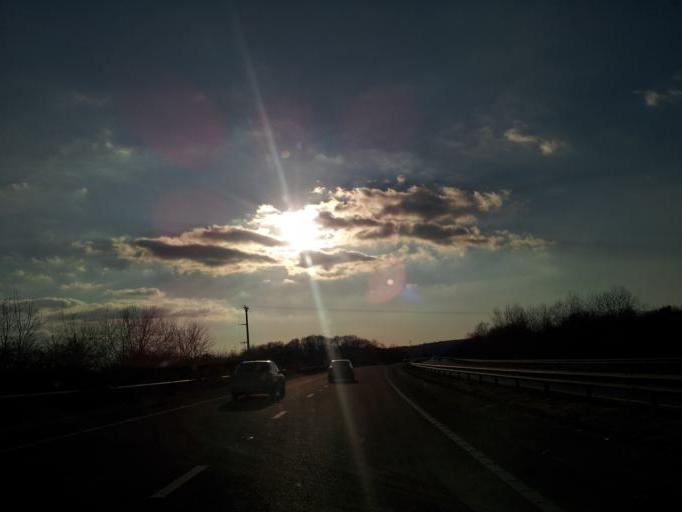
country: GB
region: England
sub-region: Devon
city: Tavistock
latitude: 50.6882
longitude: -4.1708
